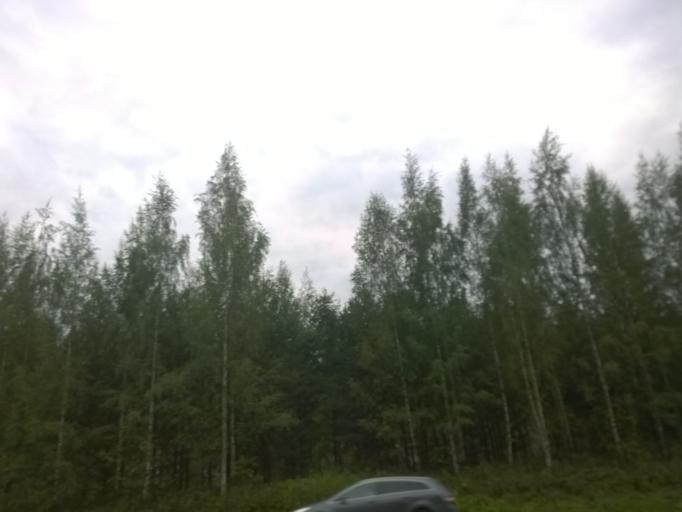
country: FI
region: Pirkanmaa
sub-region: Tampere
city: Tampere
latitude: 61.4692
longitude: 23.8411
